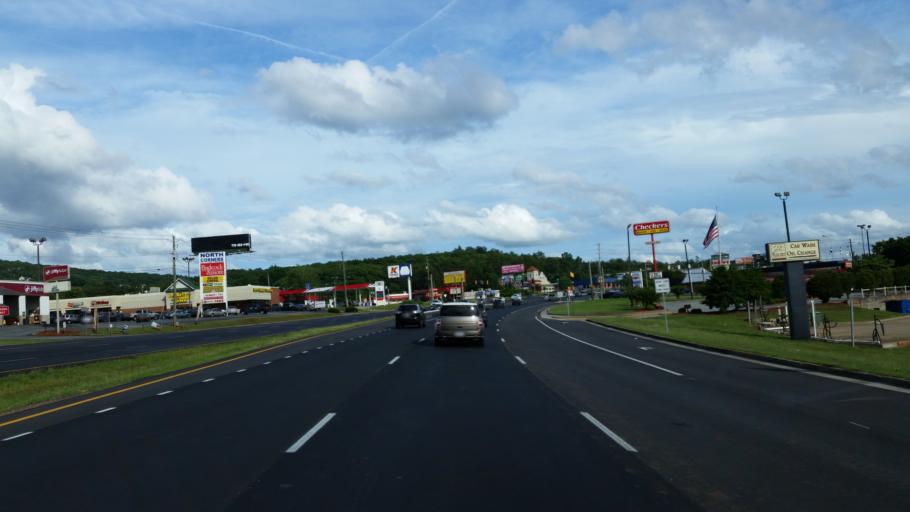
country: US
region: Georgia
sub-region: Bartow County
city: Cartersville
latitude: 34.1982
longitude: -84.7921
